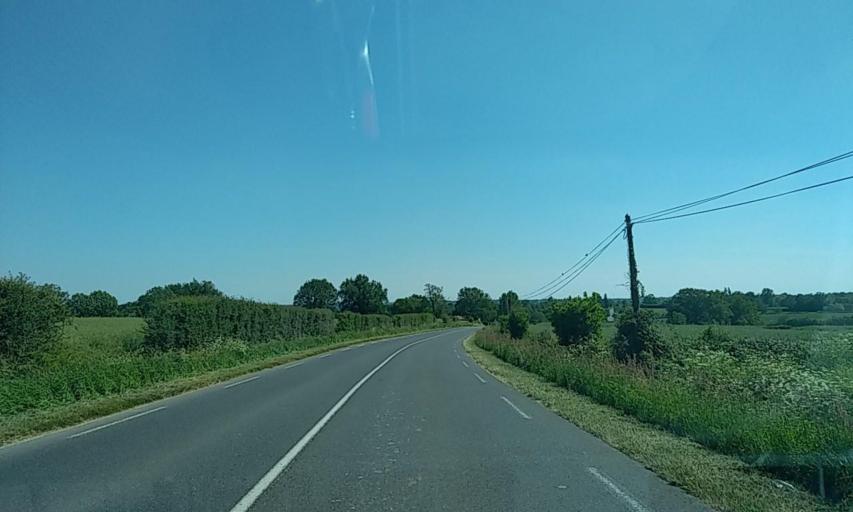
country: FR
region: Poitou-Charentes
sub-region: Departement des Deux-Sevres
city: La Chapelle-Saint-Laurent
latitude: 46.7897
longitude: -0.4806
